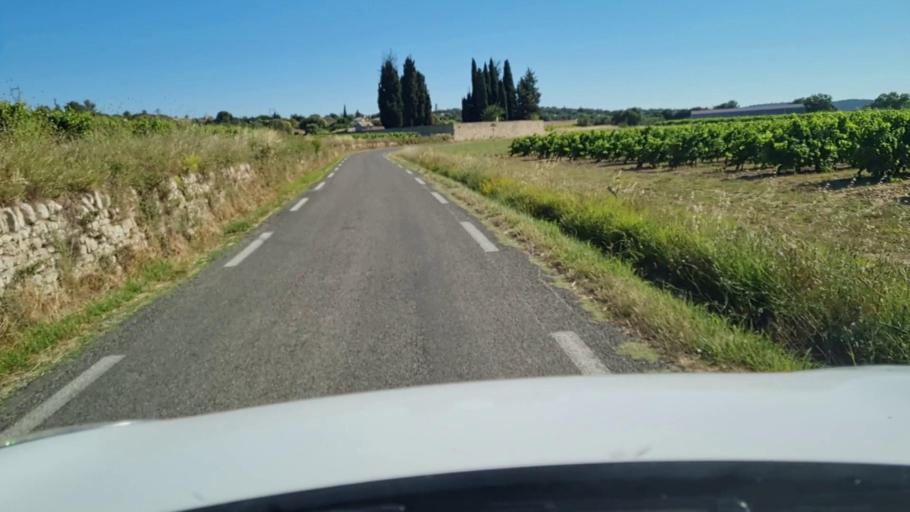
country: FR
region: Languedoc-Roussillon
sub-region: Departement du Gard
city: Sommieres
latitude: 43.8020
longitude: 4.0385
